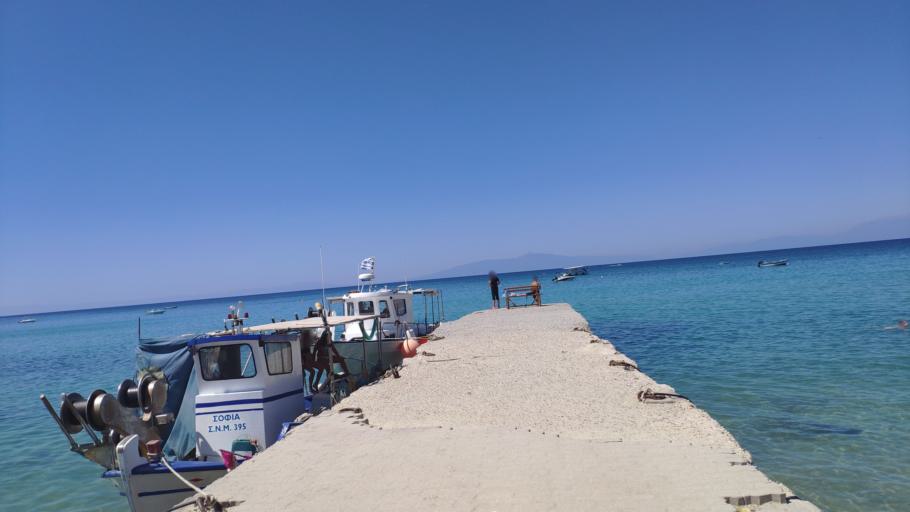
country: GR
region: Central Macedonia
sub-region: Nomos Chalkidikis
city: Kassandreia
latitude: 40.0358
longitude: 23.3595
